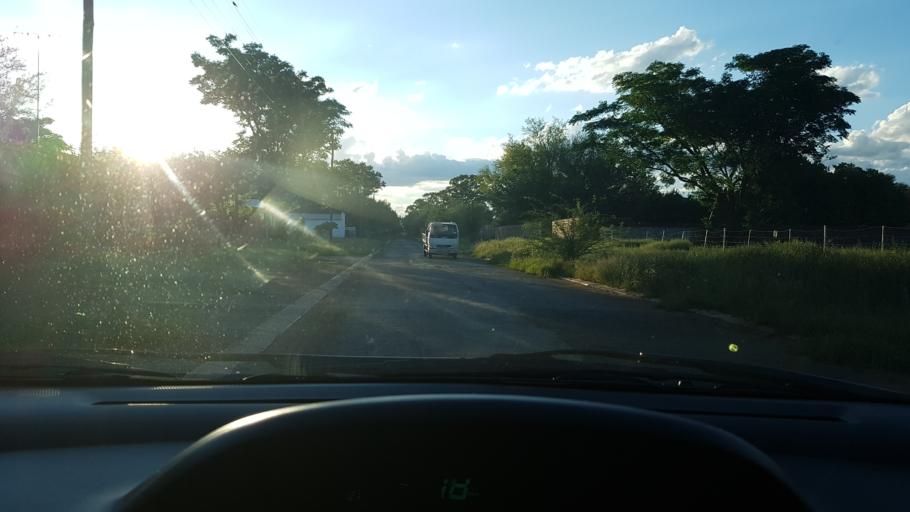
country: ZA
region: Northern Cape
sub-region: Siyanda District Municipality
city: Danielskuil
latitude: -28.1852
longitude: 23.5400
